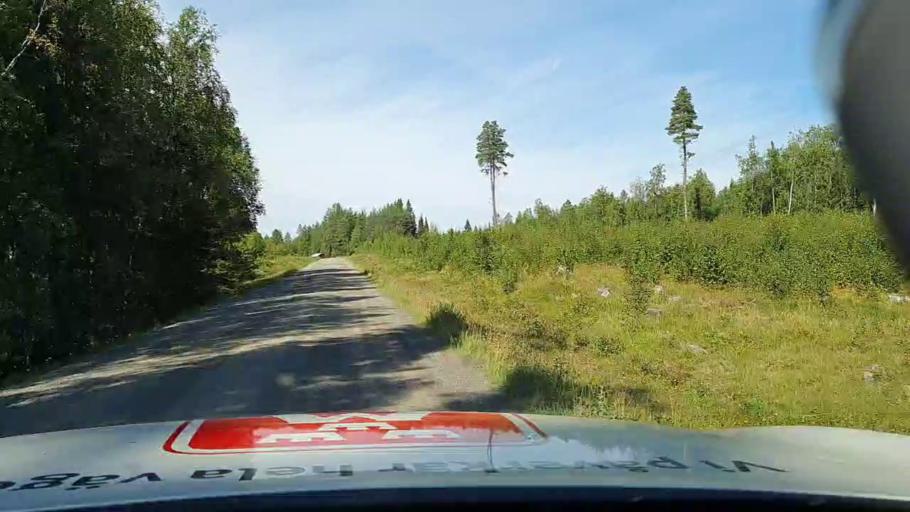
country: SE
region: Jaemtland
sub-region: Stroemsunds Kommun
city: Stroemsund
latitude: 63.7271
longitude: 15.2574
